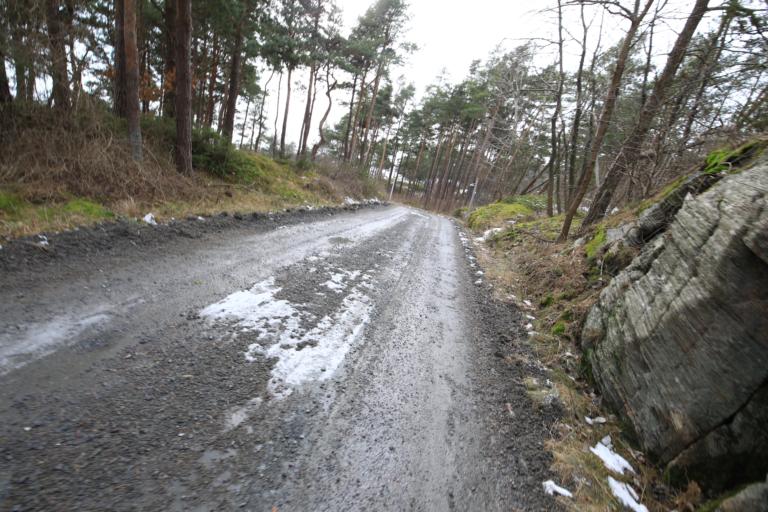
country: SE
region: Halland
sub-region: Kungsbacka Kommun
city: Frillesas
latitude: 57.2157
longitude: 12.1522
